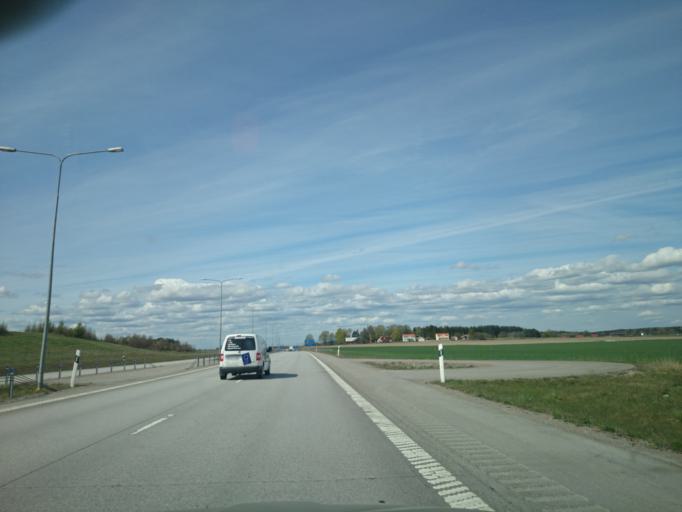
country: SE
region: Uppsala
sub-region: Uppsala Kommun
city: Saevja
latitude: 59.8742
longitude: 17.6992
